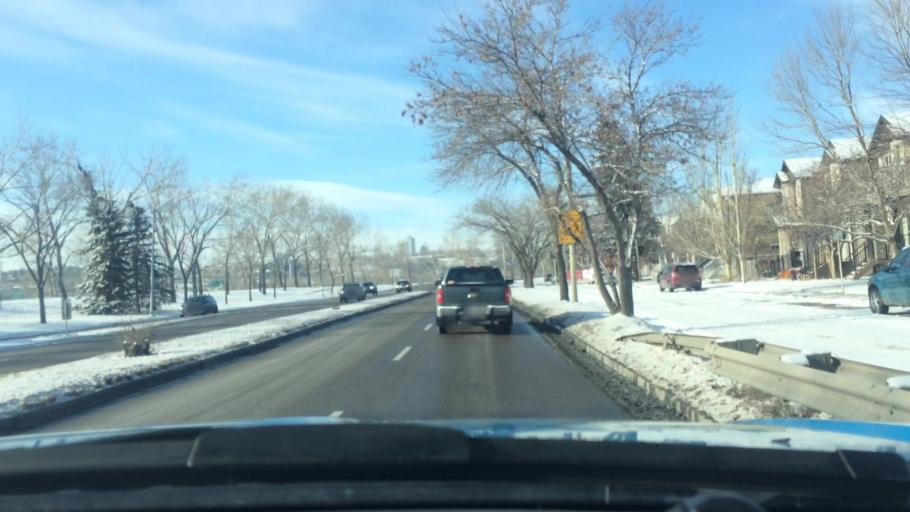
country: CA
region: Alberta
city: Calgary
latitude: 51.0493
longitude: -114.0964
